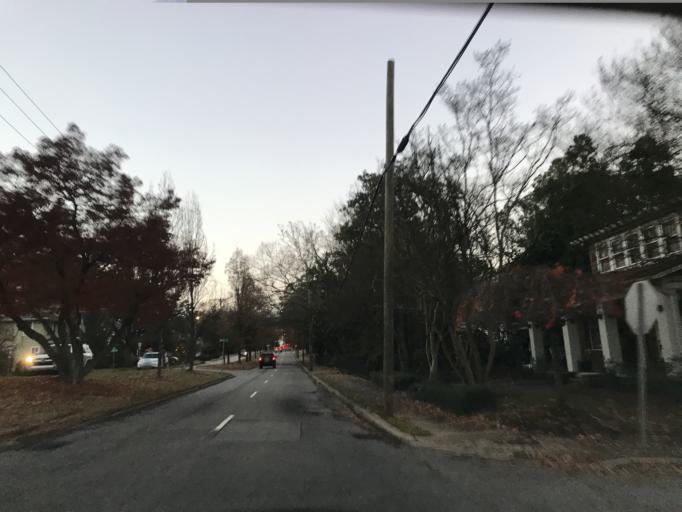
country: US
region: North Carolina
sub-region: Wake County
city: West Raleigh
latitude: 35.8066
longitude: -78.6472
